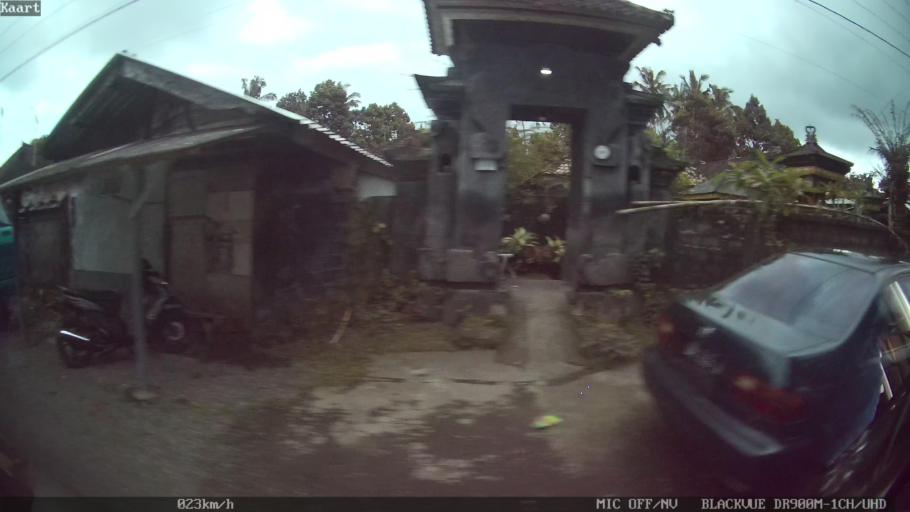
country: ID
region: Bali
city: Banjar Wangsian
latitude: -8.4481
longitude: 115.4230
